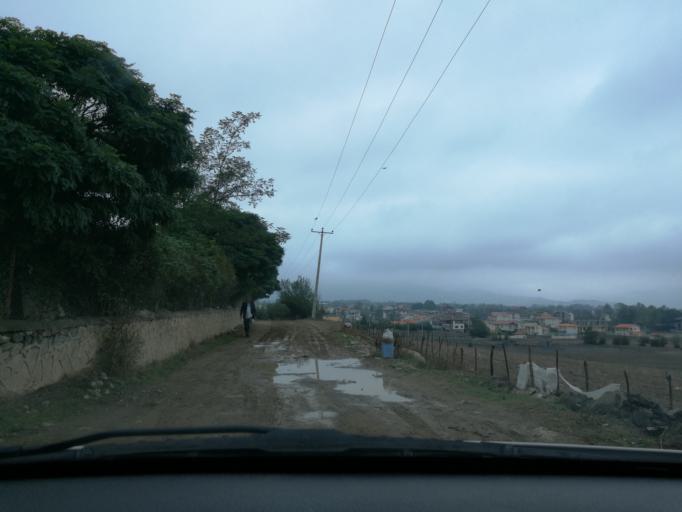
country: IR
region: Mazandaran
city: `Abbasabad
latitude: 36.5027
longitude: 51.2060
